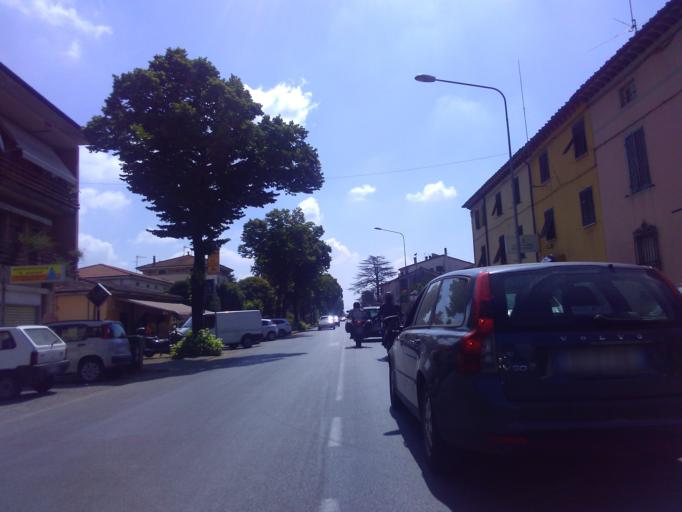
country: IT
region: Tuscany
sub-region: Provincia di Lucca
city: Lucca
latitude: 43.8482
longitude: 10.4683
